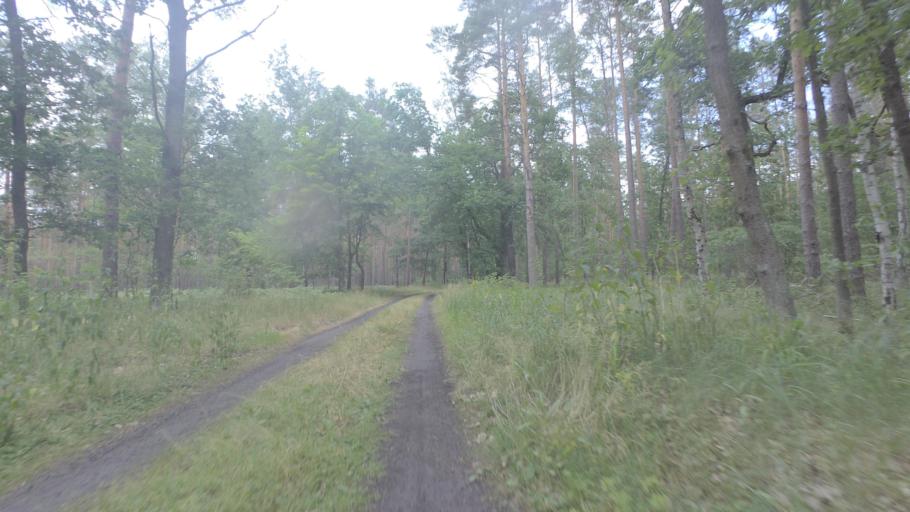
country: DE
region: Brandenburg
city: Am Mellensee
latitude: 52.1296
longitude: 13.4430
